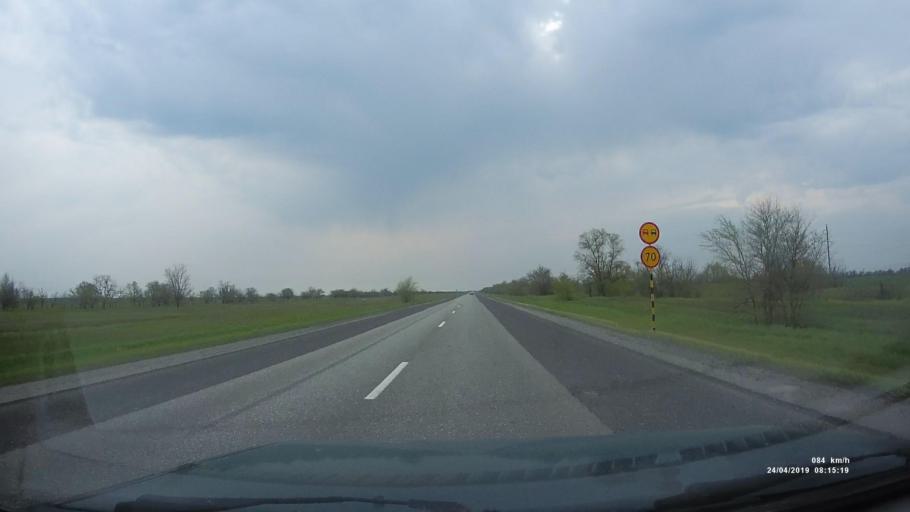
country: RU
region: Kalmykiya
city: Priyutnoye
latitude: 46.1002
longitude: 43.5922
